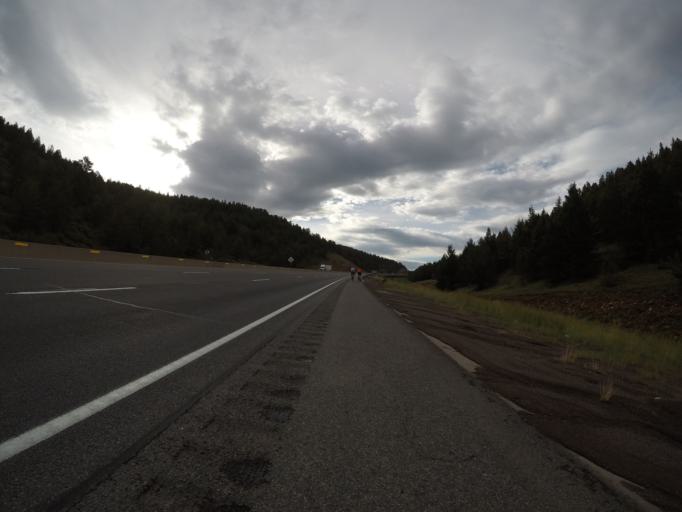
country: US
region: Wyoming
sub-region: Albany County
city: Laramie
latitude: 41.2616
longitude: -105.4598
